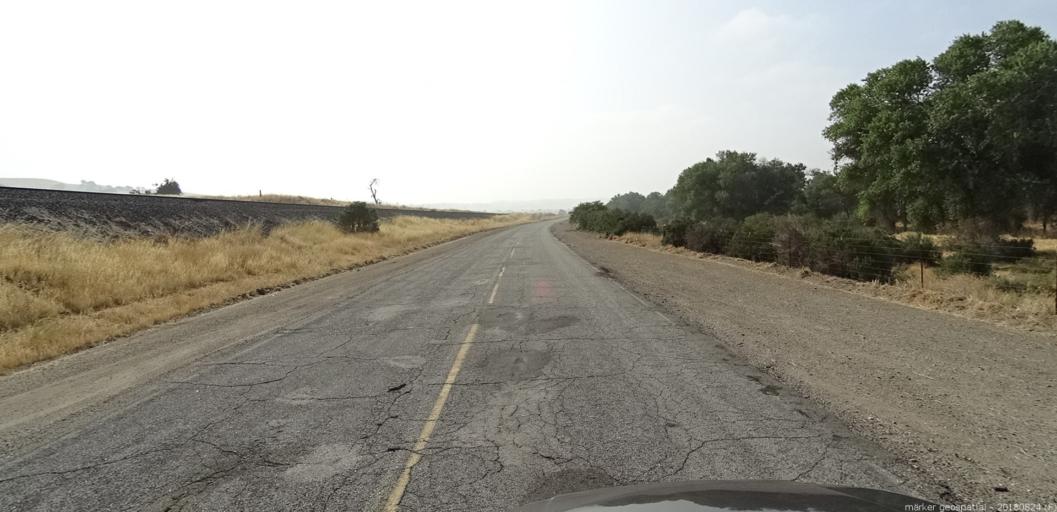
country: US
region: California
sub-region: San Luis Obispo County
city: San Miguel
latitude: 35.8595
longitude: -120.7659
